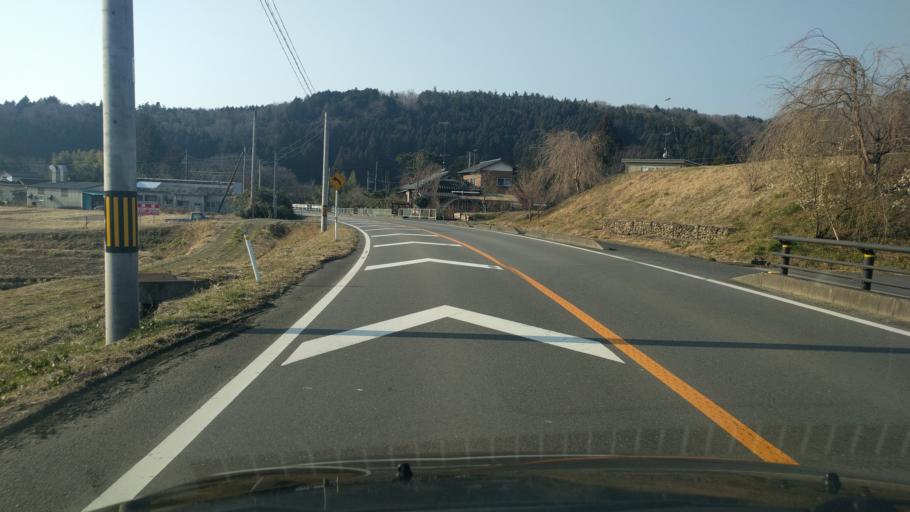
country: JP
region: Fukushima
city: Iwaki
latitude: 37.0768
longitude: 140.8024
